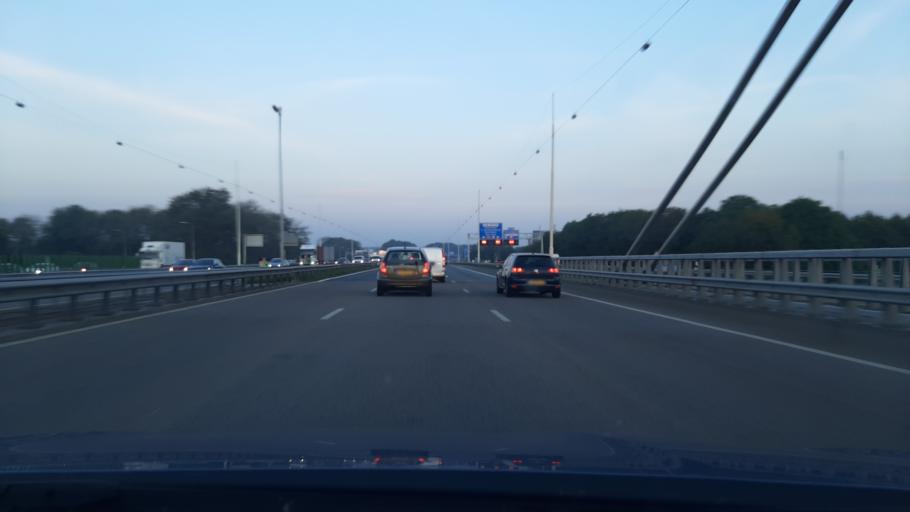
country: NL
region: Utrecht
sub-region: Gemeente Nieuwegein
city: Nieuwegein
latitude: 52.0615
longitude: 5.0973
